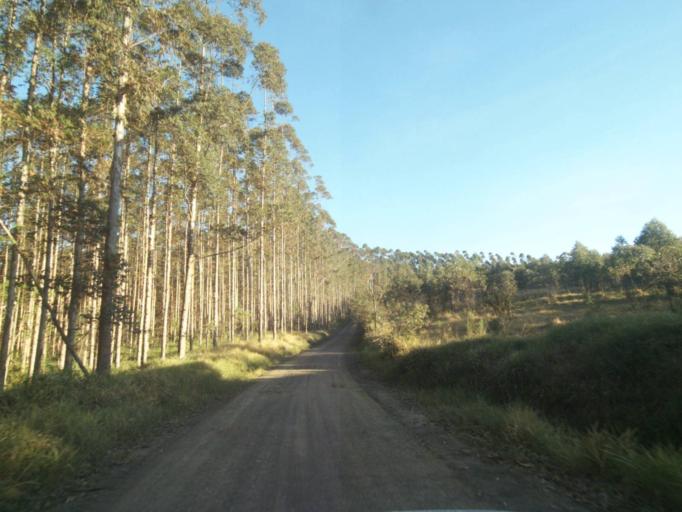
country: BR
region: Parana
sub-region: Telemaco Borba
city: Telemaco Borba
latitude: -24.4900
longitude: -50.5943
